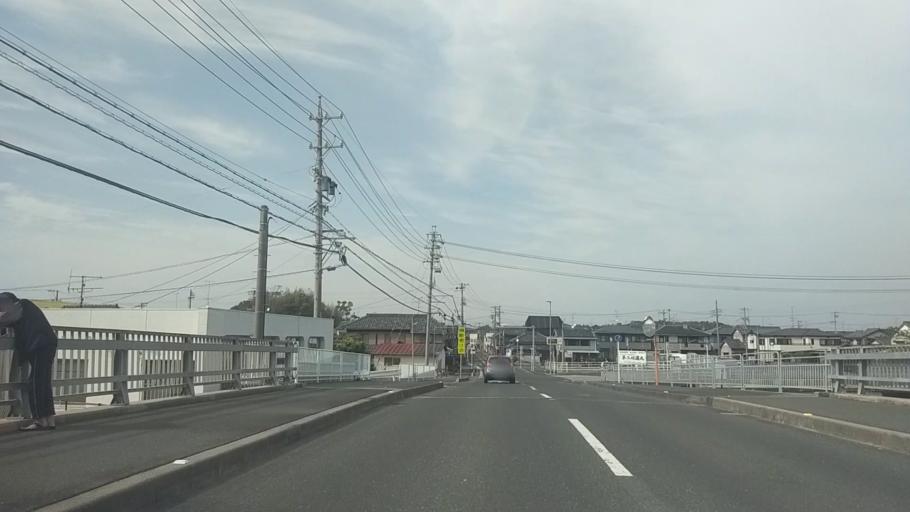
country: JP
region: Shizuoka
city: Kosai-shi
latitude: 34.7209
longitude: 137.5925
